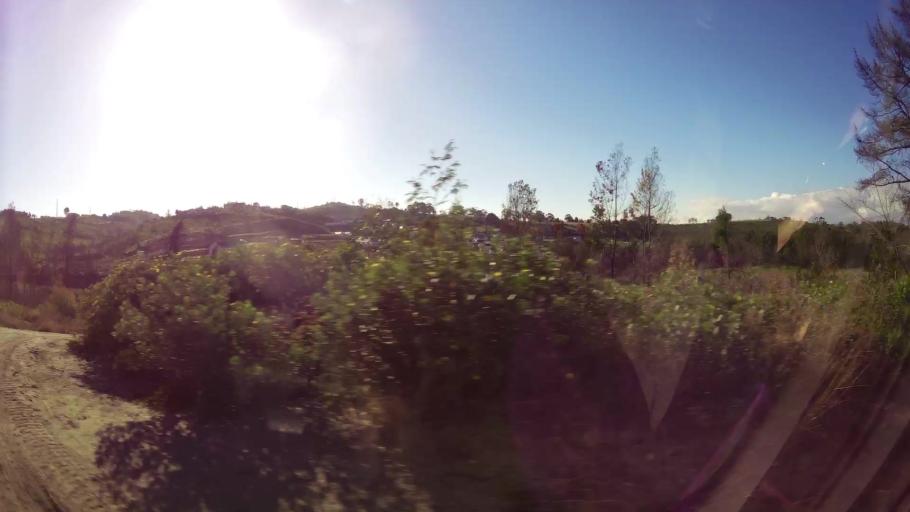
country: ZA
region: Western Cape
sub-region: Eden District Municipality
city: Knysna
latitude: -34.0256
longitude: 23.0088
